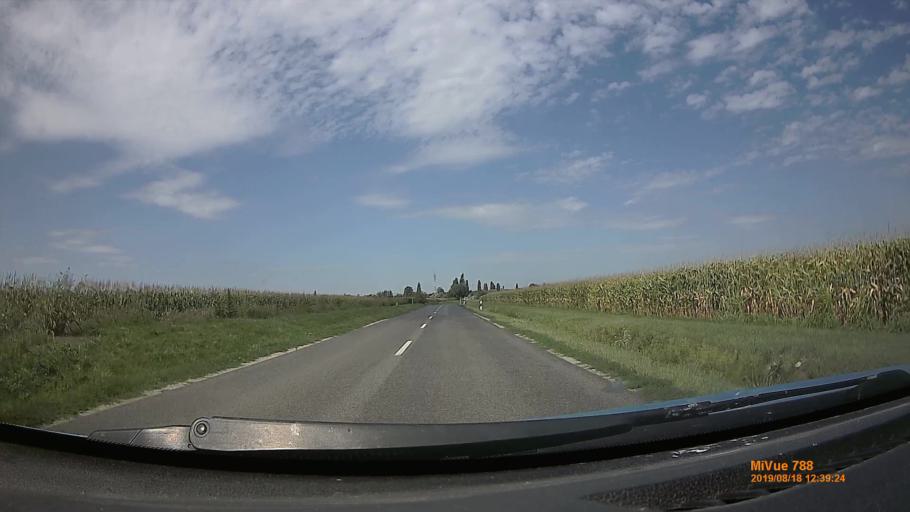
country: HU
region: Fejer
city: Szabadbattyan
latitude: 47.0979
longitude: 18.3901
